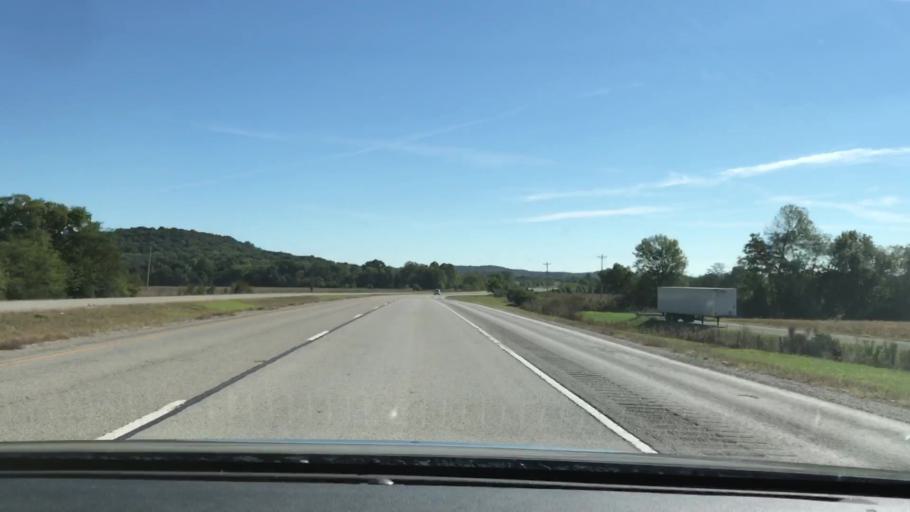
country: US
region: Kentucky
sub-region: Todd County
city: Elkton
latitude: 36.8457
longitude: -87.2816
